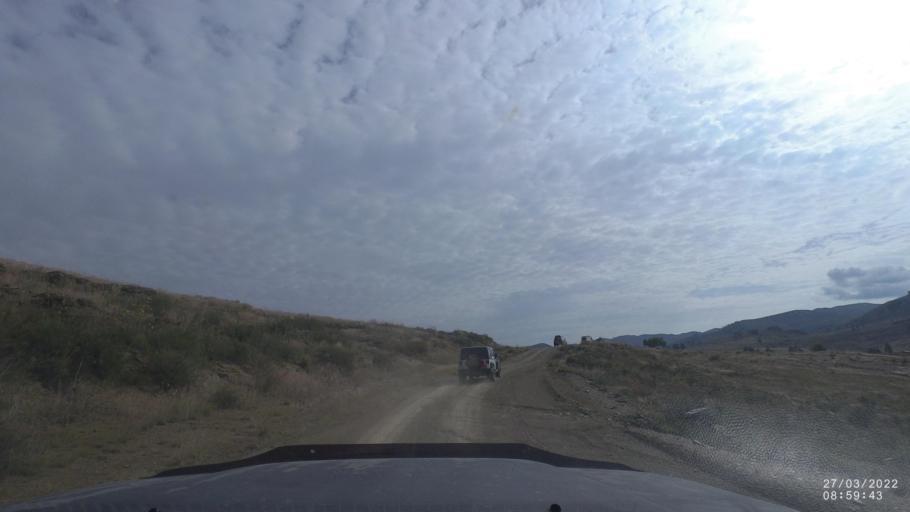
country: BO
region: Cochabamba
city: Cliza
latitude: -17.7383
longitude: -65.8541
